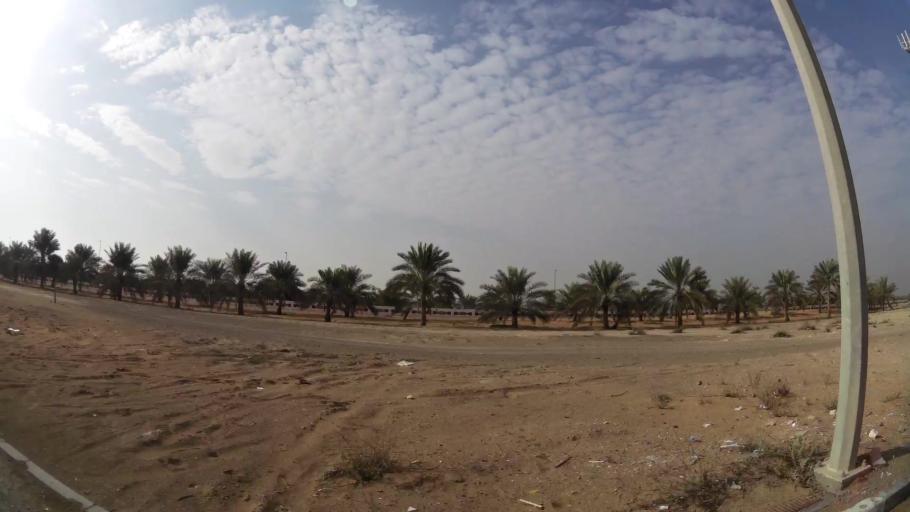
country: AE
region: Abu Dhabi
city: Abu Dhabi
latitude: 24.2393
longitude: 54.7190
